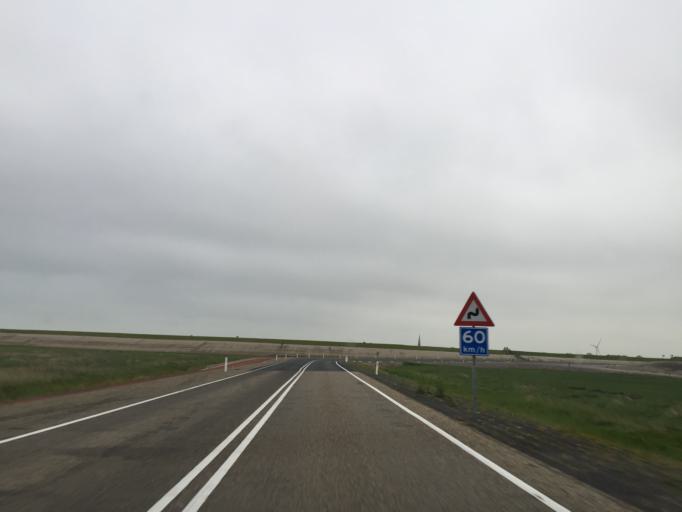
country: NL
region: Friesland
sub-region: Gemeente Dongeradeel
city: Holwerd
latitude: 53.3823
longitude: 5.8910
